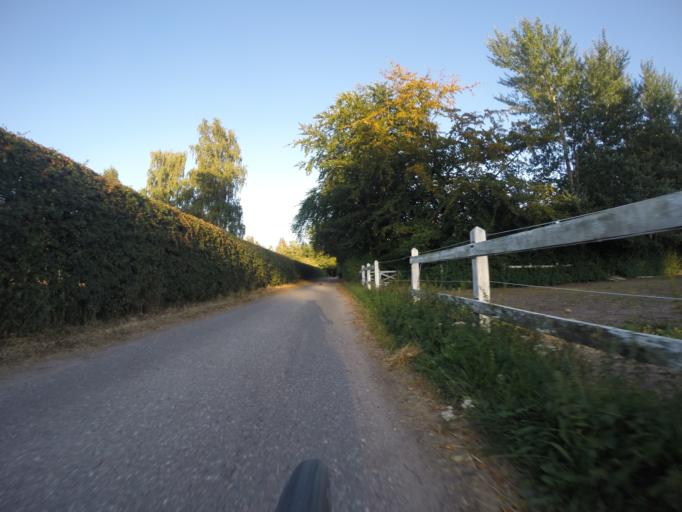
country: DK
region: Capital Region
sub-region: Ballerup Kommune
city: Ballerup
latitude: 55.7015
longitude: 12.3317
